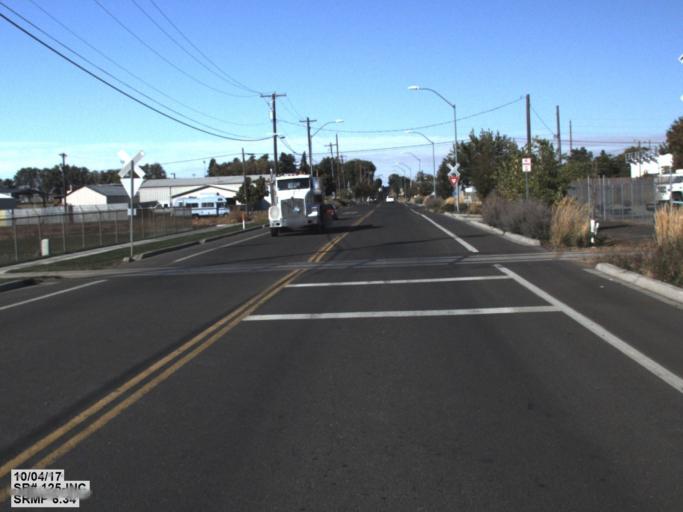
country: US
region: Washington
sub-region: Walla Walla County
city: Walla Walla
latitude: 46.0723
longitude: -118.3565
